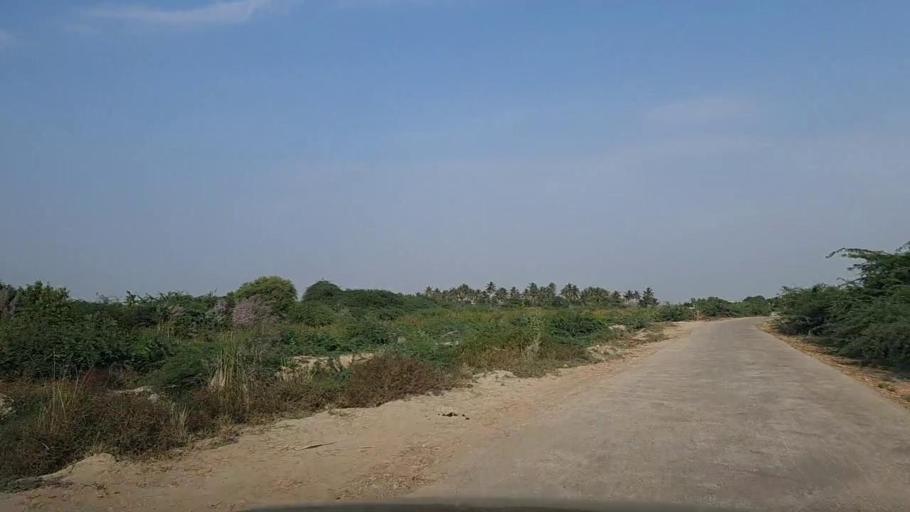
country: PK
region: Sindh
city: Thatta
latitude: 24.6512
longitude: 67.9123
